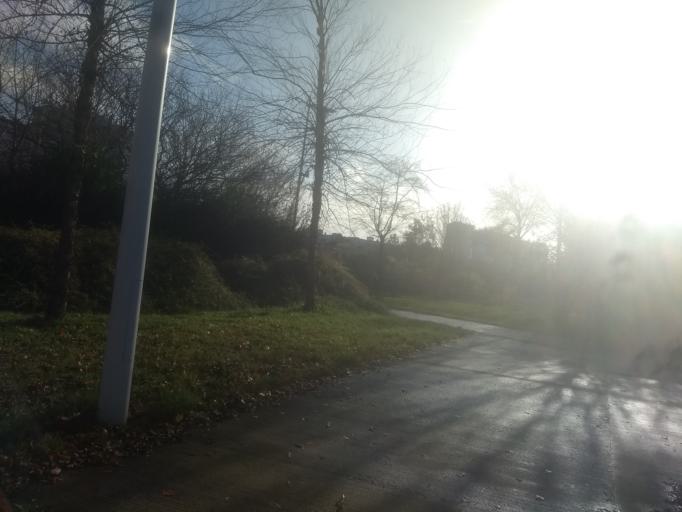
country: FR
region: Nord-Pas-de-Calais
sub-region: Departement du Pas-de-Calais
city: Anzin-Saint-Aubin
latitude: 50.3031
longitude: 2.7406
